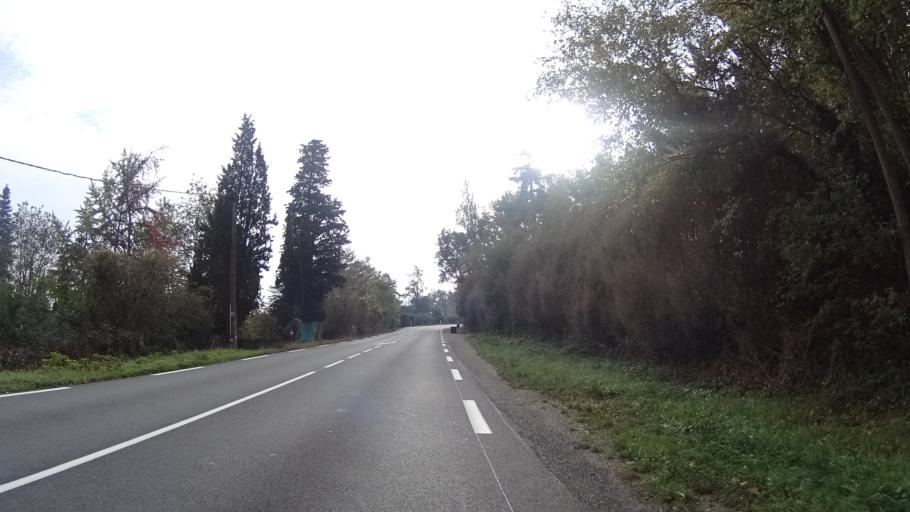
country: FR
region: Aquitaine
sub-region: Departement du Lot-et-Garonne
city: Boe
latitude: 44.1561
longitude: 0.6272
